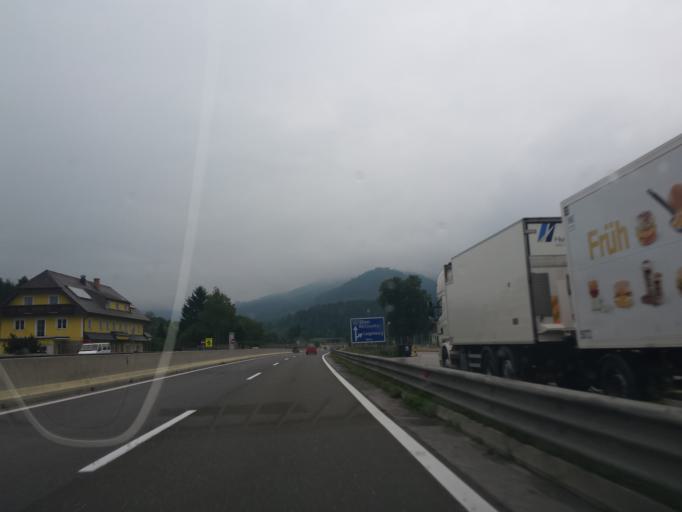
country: AT
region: Styria
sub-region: Politischer Bezirk Bruck-Muerzzuschlag
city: Langenwang
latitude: 47.5585
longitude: 15.5928
